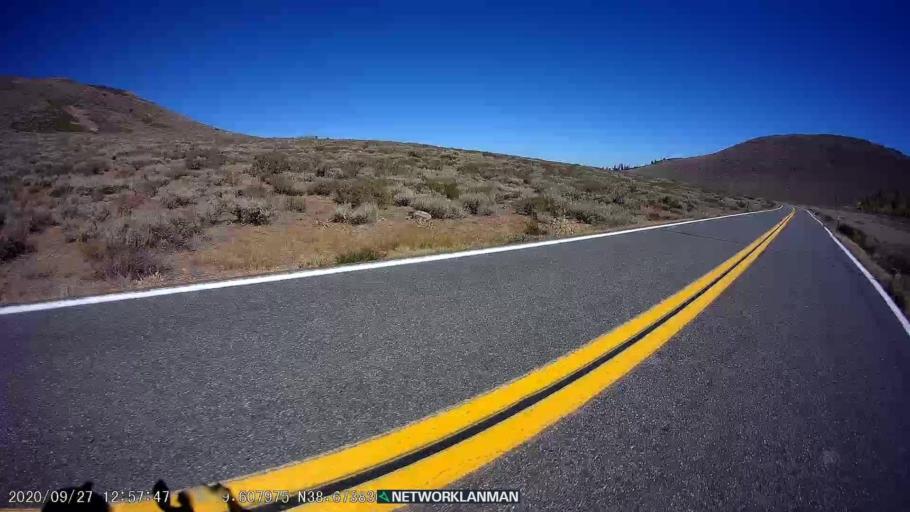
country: US
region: Nevada
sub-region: Douglas County
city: Gardnerville Ranchos
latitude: 38.6739
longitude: -119.6078
